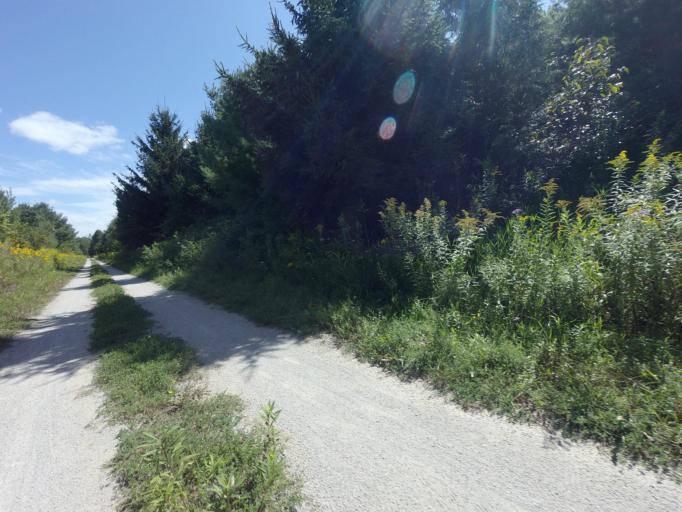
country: CA
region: Ontario
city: Orangeville
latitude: 43.7771
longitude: -80.1140
